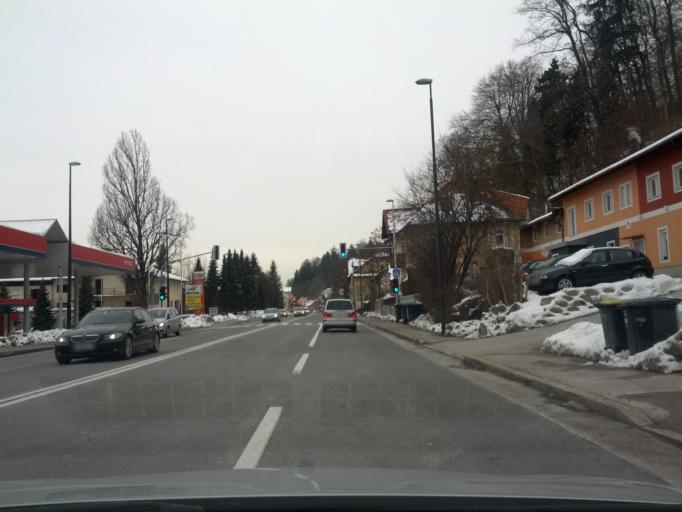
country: SI
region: Ljubljana
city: Ljubljana
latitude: 46.0334
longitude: 14.5275
